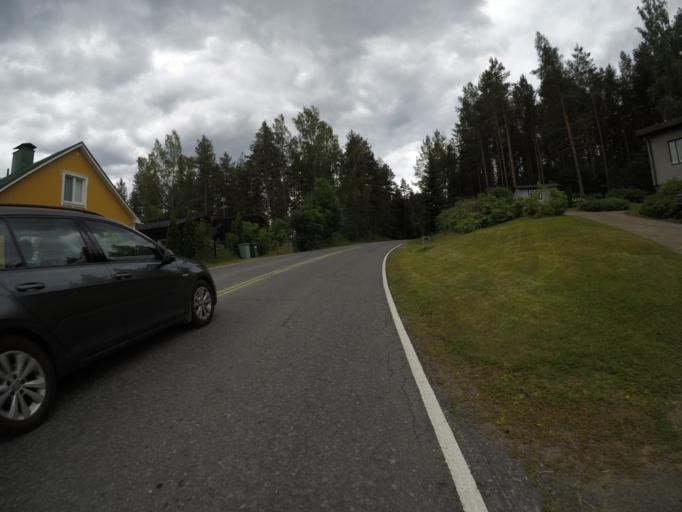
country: FI
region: Haeme
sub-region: Haemeenlinna
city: Haemeenlinna
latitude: 60.9802
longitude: 24.4522
